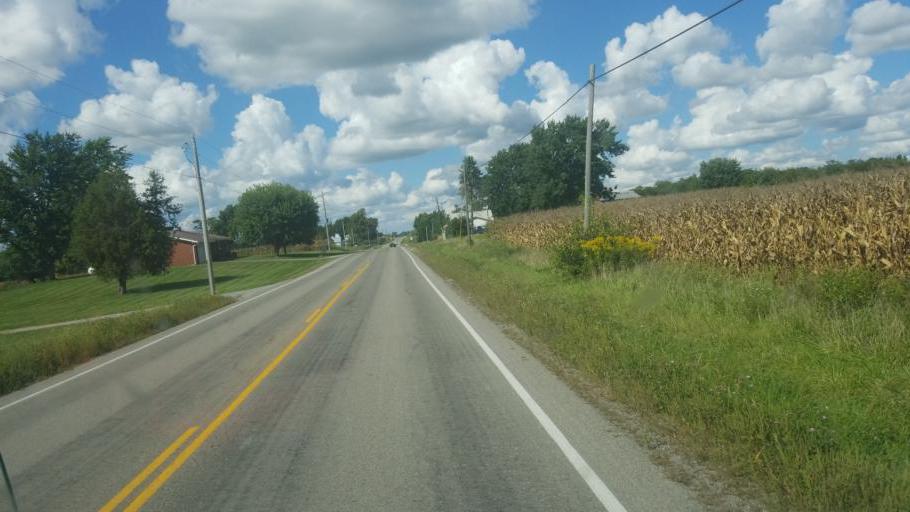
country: US
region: Ohio
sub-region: Hardin County
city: Kenton
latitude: 40.5211
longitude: -83.5743
